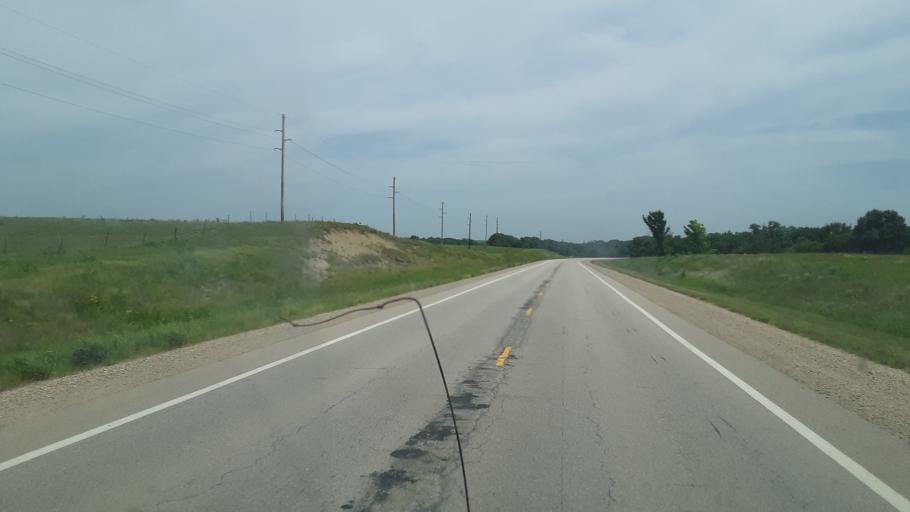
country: US
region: Kansas
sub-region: Greenwood County
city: Eureka
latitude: 37.8387
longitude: -96.1095
